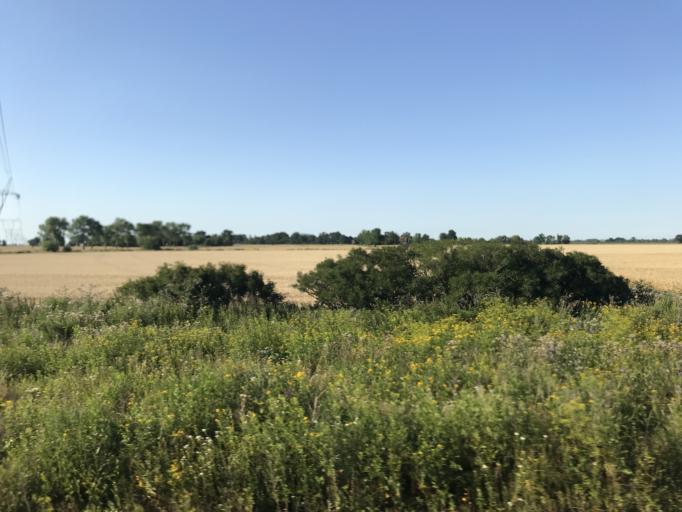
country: PL
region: Pomeranian Voivodeship
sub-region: Powiat malborski
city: Miloradz
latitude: 54.0698
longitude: 18.9420
